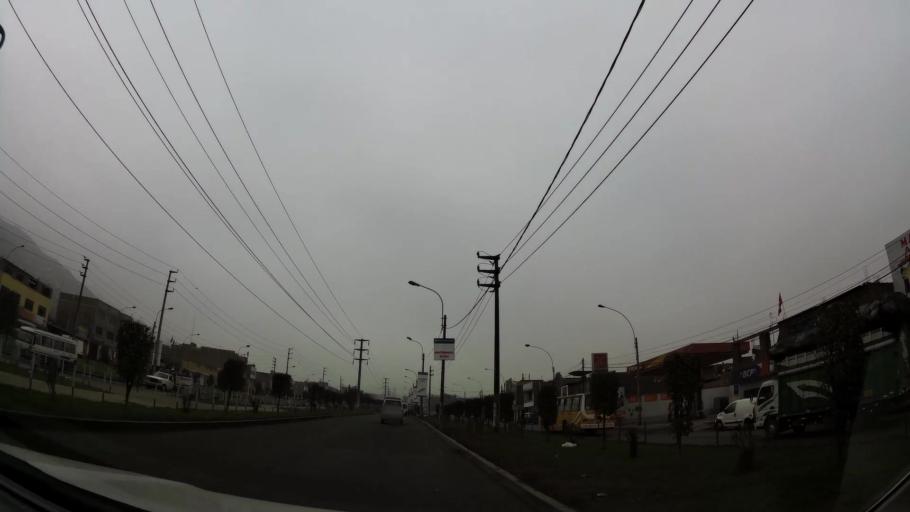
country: PE
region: Lima
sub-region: Lima
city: Urb. Santo Domingo
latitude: -11.9363
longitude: -76.9709
